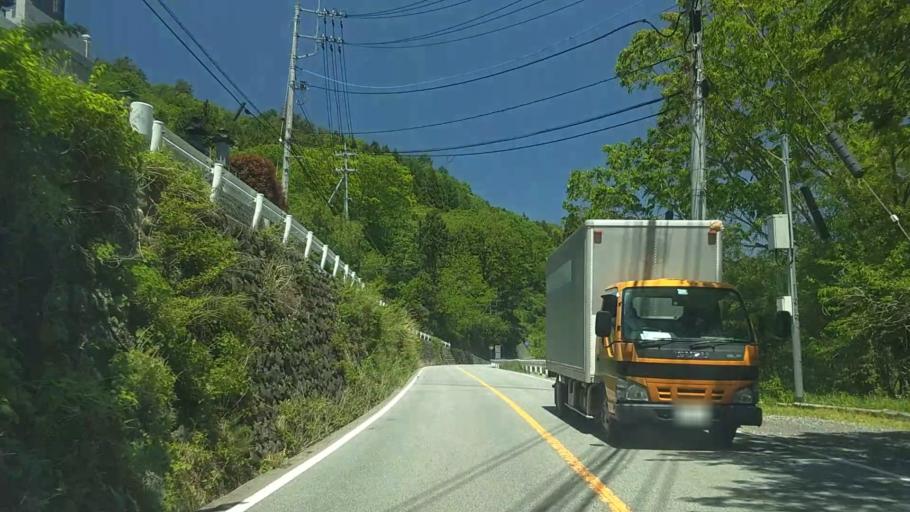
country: JP
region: Yamanashi
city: Nirasaki
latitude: 35.8746
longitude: 138.4289
